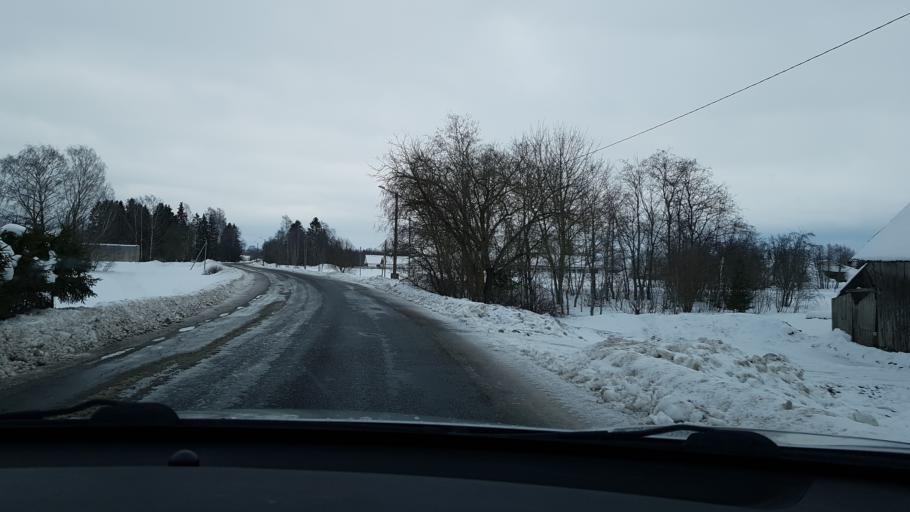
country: EE
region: Jaervamaa
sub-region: Koeru vald
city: Koeru
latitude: 58.9722
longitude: 26.0090
